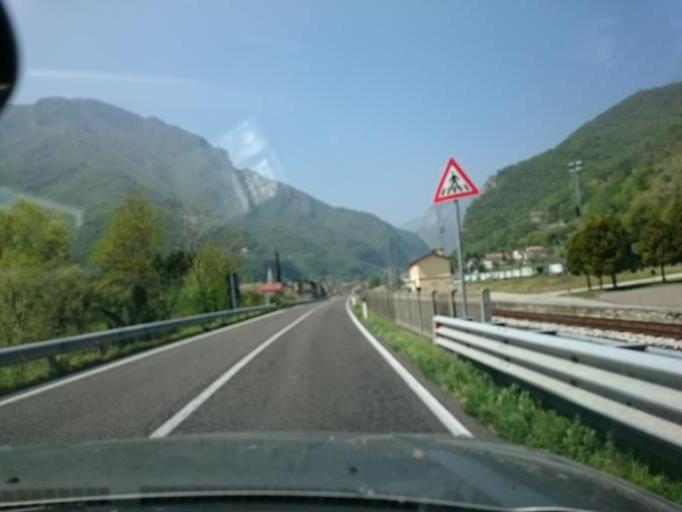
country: IT
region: Veneto
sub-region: Provincia di Vicenza
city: San Nazario
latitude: 45.8427
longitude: 11.6801
